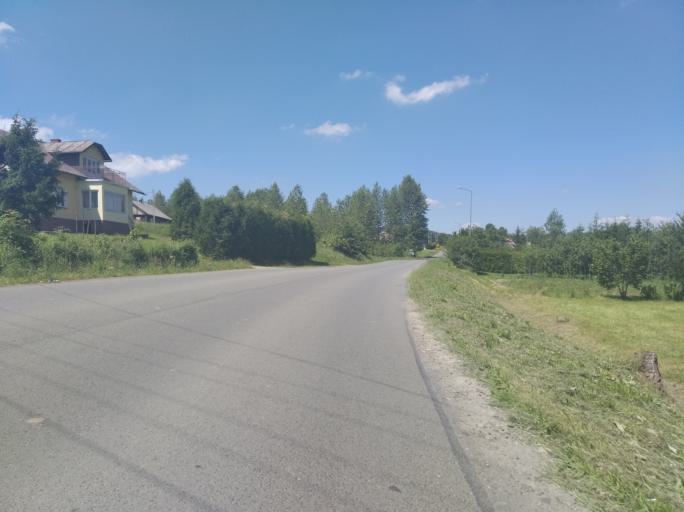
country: PL
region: Subcarpathian Voivodeship
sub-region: Powiat brzozowski
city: Jablonka
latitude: 49.6965
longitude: 22.1378
